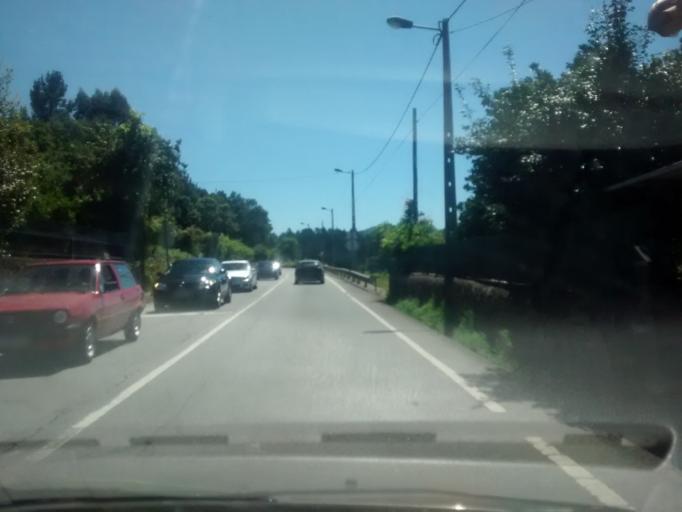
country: PT
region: Braga
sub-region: Barcelos
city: Galegos
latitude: 41.5258
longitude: -8.5647
